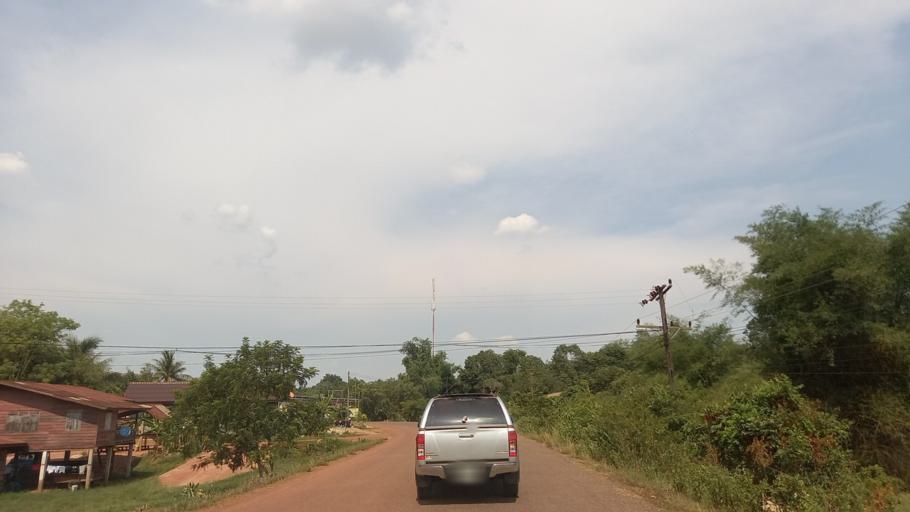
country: LA
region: Bolikhamxai
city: Muang Pakxan
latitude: 18.4278
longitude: 103.7154
